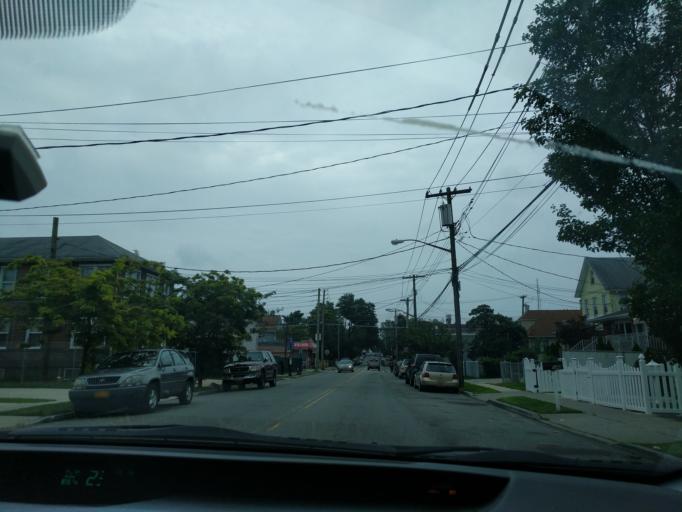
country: US
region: New York
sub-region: Richmond County
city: Bloomfield
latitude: 40.6365
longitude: -74.1662
